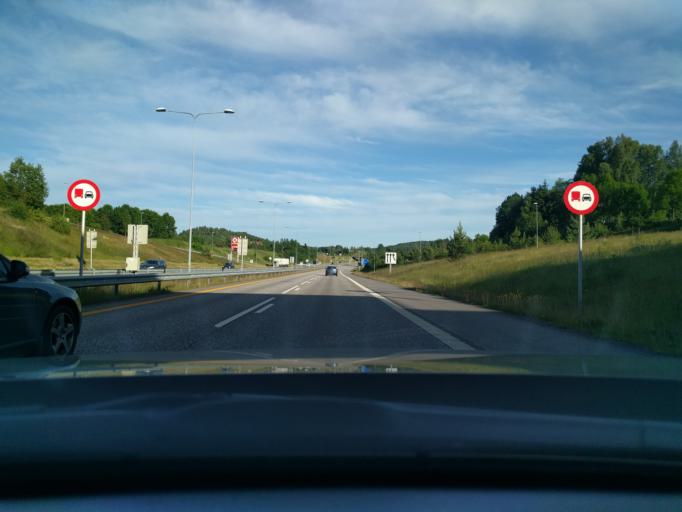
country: NO
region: Vestfold
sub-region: Holmestrand
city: Gullhaug
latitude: 59.5139
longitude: 10.2034
